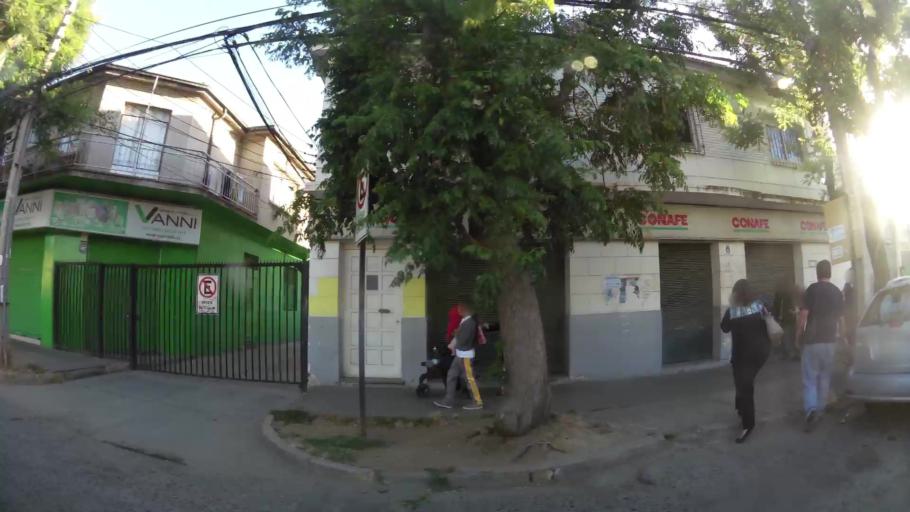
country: CL
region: Valparaiso
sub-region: Provincia de Valparaiso
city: Vina del Mar
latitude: -33.0251
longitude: -71.5453
